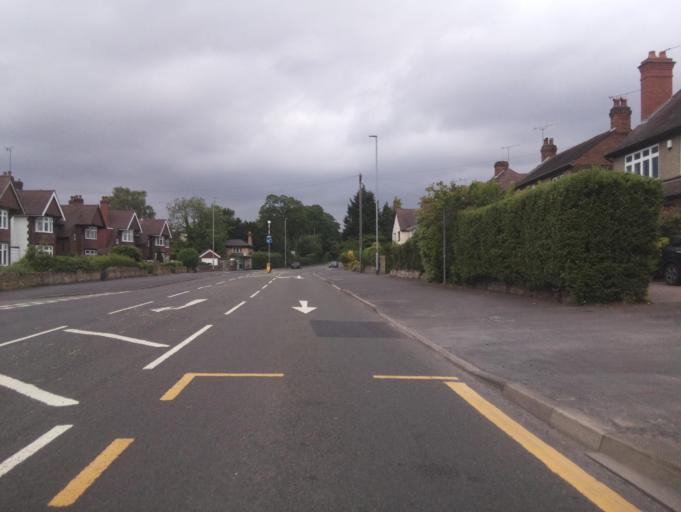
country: GB
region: England
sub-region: Staffordshire
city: Stafford
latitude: 52.7919
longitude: -2.1193
